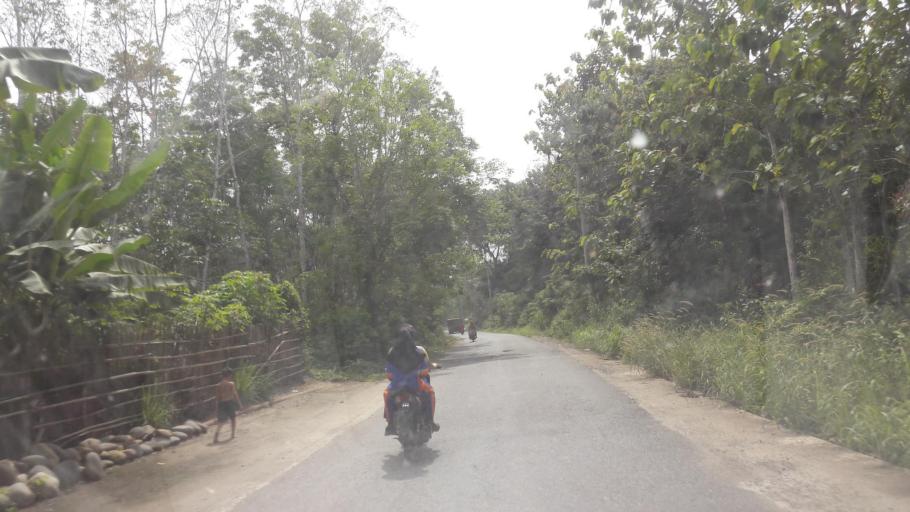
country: ID
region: South Sumatra
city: Gunungmenang
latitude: -3.2011
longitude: 104.1077
